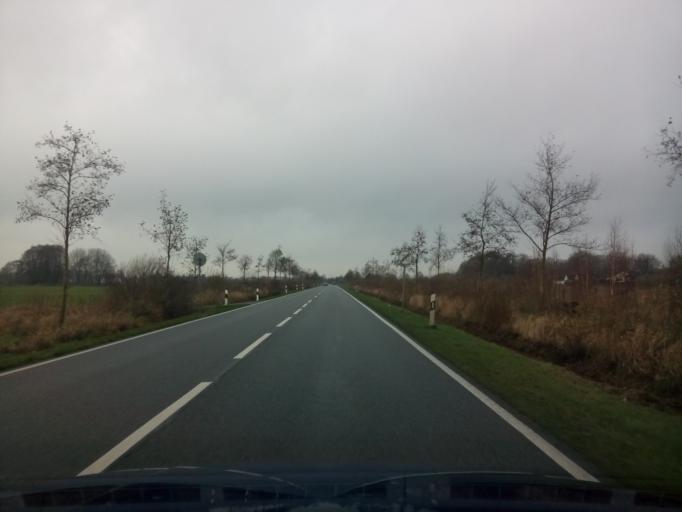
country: DE
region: Lower Saxony
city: Lilienthal
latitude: 53.1563
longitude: 8.9358
